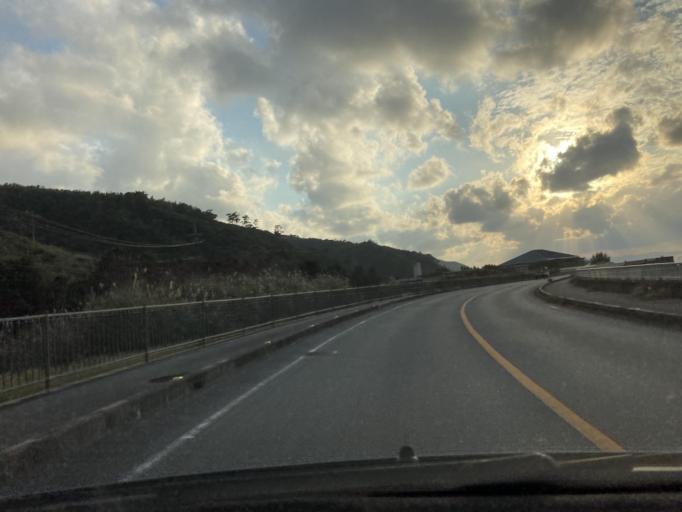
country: JP
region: Okinawa
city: Nago
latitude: 26.7885
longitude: 128.2236
